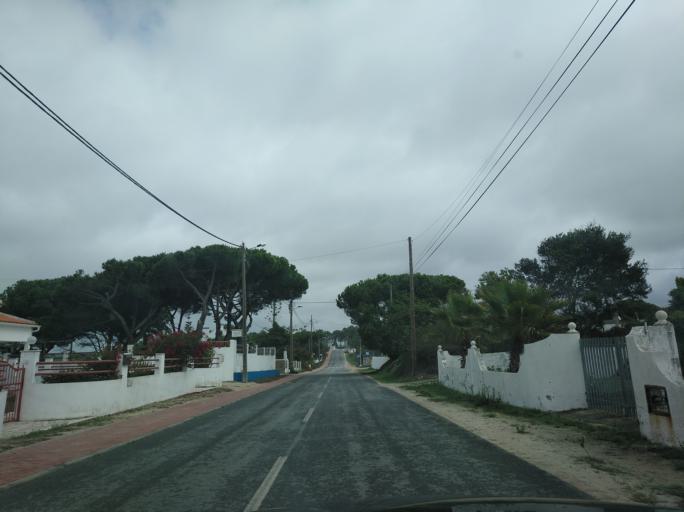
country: PT
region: Setubal
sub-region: Santiago do Cacem
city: Santo Andre
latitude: 38.1293
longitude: -8.7861
